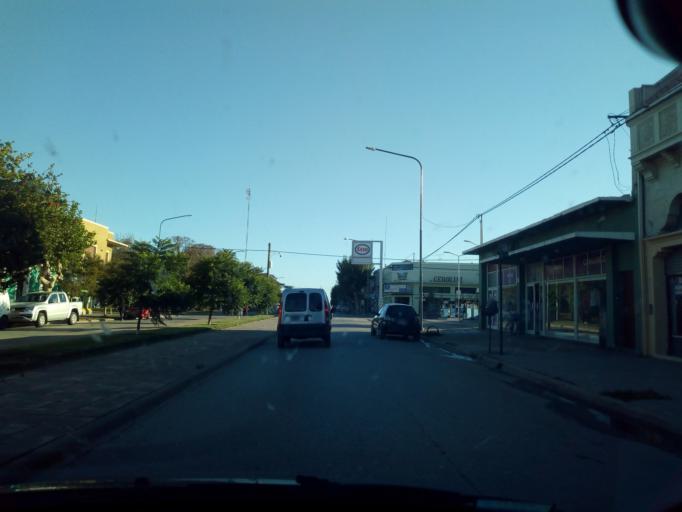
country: AR
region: Buenos Aires
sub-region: Partido de Loberia
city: Loberia
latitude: -38.1622
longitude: -58.7814
